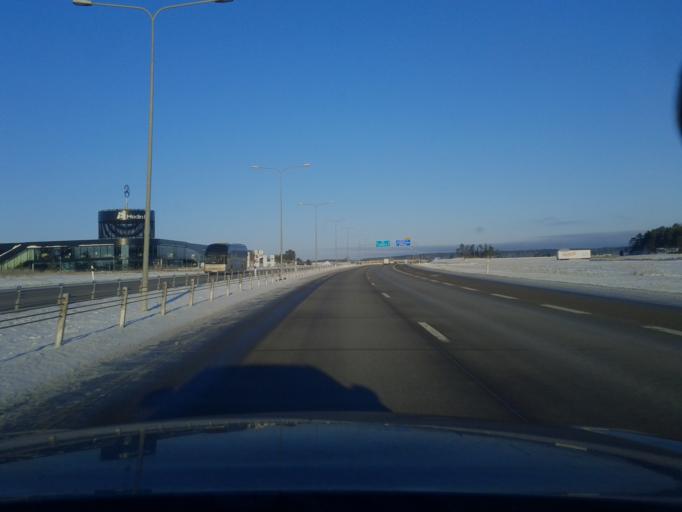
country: SE
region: Uppsala
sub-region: Uppsala Kommun
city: Saevja
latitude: 59.8377
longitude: 17.7324
